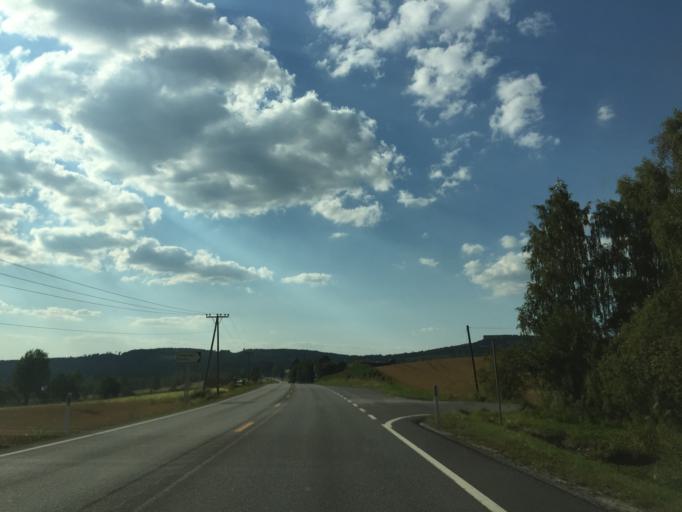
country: NO
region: Hedmark
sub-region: Kongsvinger
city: Kongsvinger
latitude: 60.2120
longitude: 11.9573
